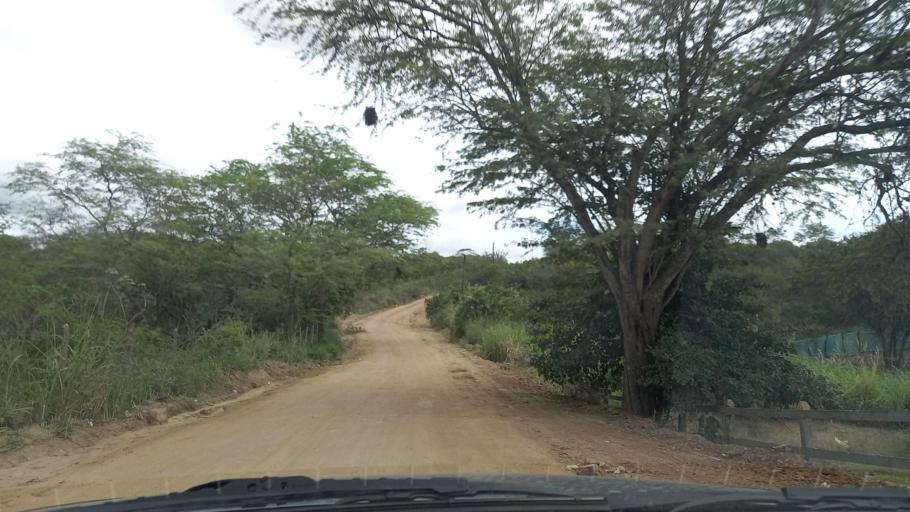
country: BR
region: Pernambuco
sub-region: Gravata
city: Gravata
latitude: -8.1822
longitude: -35.5880
